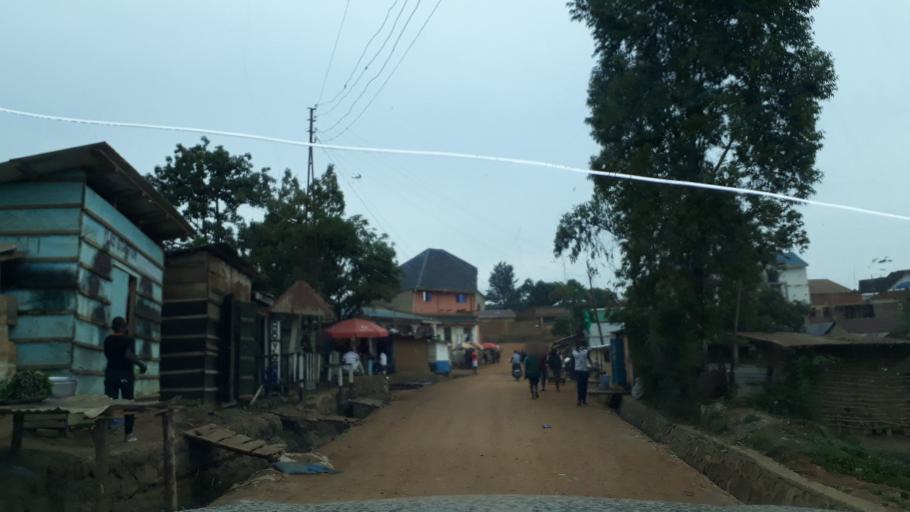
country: CD
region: Eastern Province
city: Bunia
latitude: 1.5642
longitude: 30.2464
